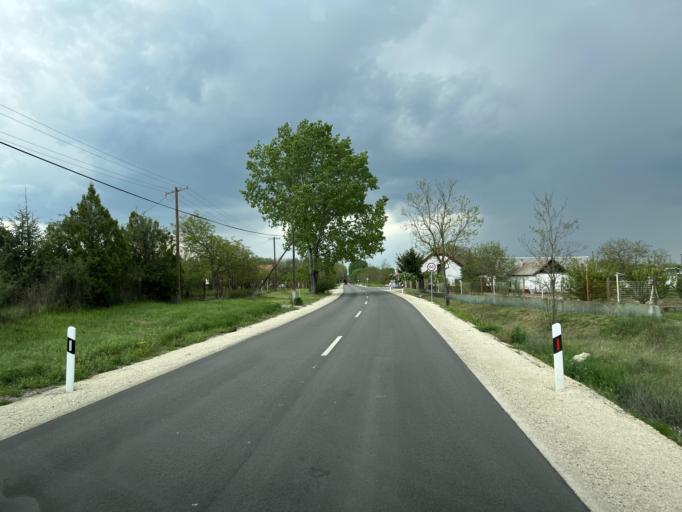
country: HU
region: Pest
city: Nagykoros
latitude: 47.0400
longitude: 19.7480
